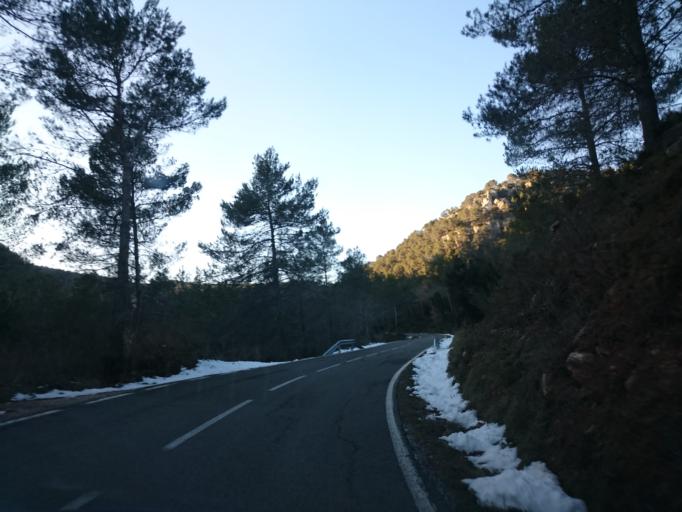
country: ES
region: Catalonia
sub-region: Provincia de Tarragona
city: Querol
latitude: 41.3783
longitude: 1.4777
